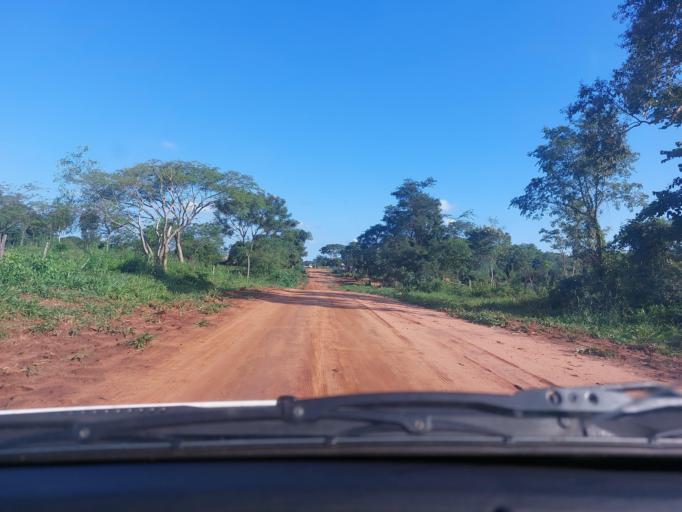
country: PY
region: San Pedro
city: Guayaybi
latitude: -24.5295
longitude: -56.5455
